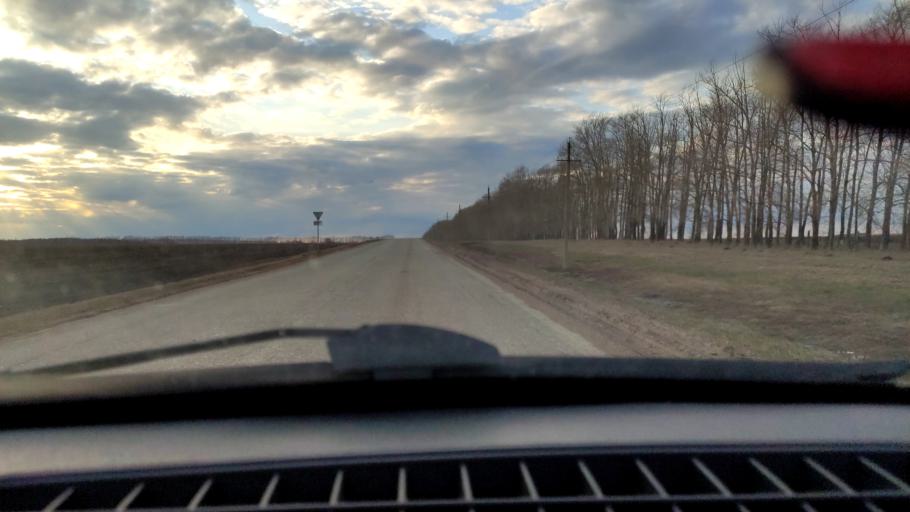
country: RU
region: Bashkortostan
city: Tolbazy
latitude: 53.9855
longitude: 55.7970
